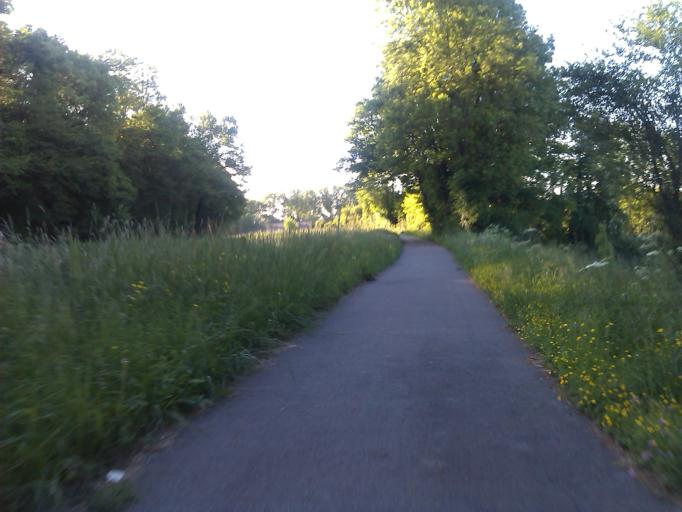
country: FR
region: Auvergne
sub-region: Departement de l'Allier
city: Dompierre-sur-Besbre
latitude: 46.5361
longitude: 3.7136
